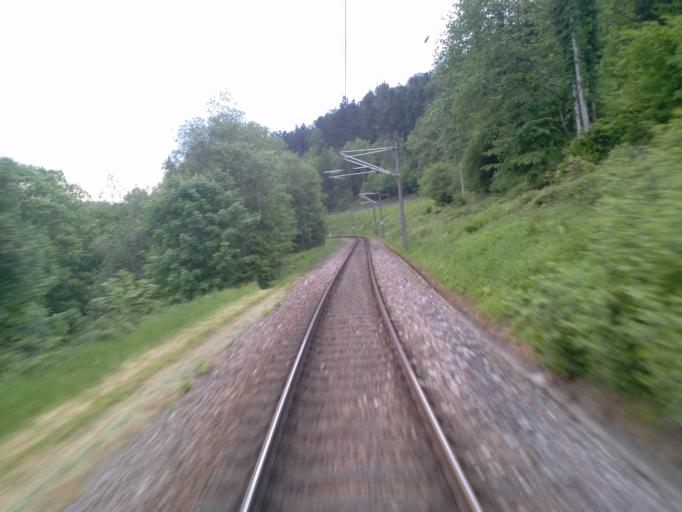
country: DE
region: Baden-Wuerttemberg
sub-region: Karlsruhe Region
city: Bad Herrenalb
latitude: 48.8393
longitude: 8.4402
